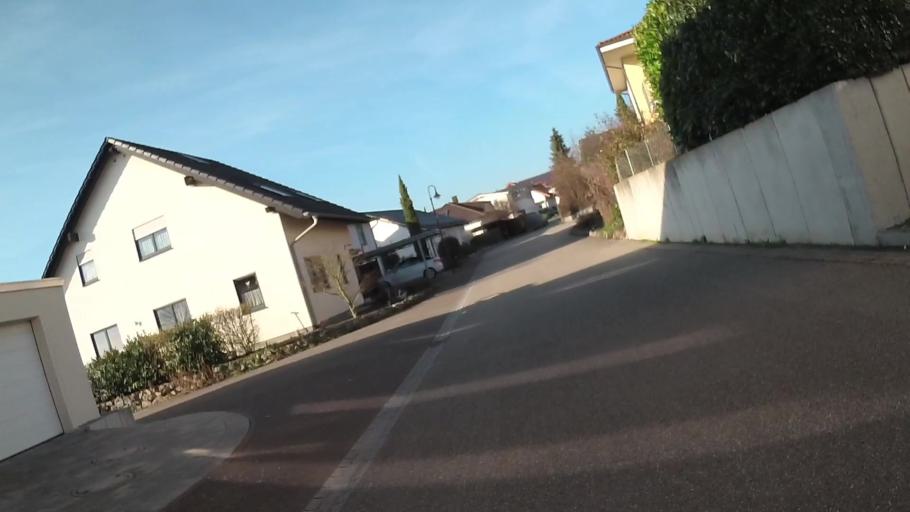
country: DE
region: Baden-Wuerttemberg
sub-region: Karlsruhe Region
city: Malsch
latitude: 49.2422
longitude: 8.6822
